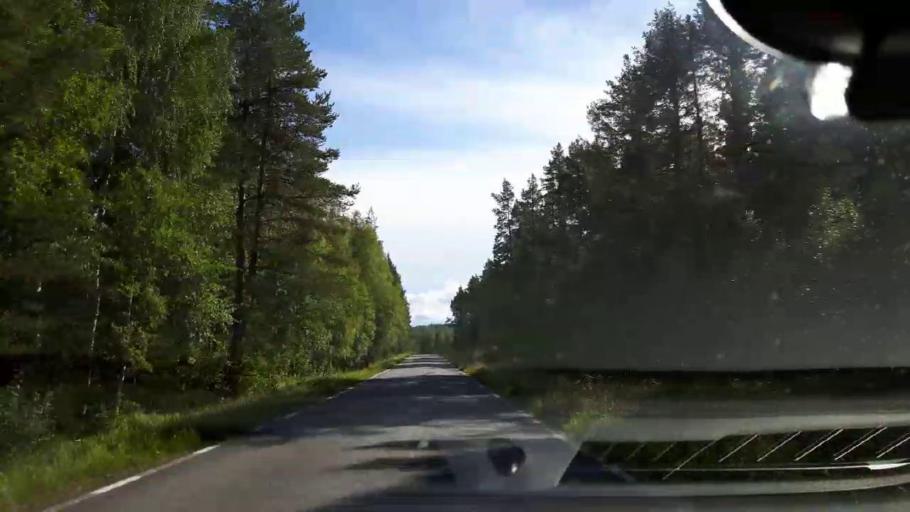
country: SE
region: Jaemtland
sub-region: OEstersunds Kommun
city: Lit
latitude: 63.2308
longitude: 15.2638
